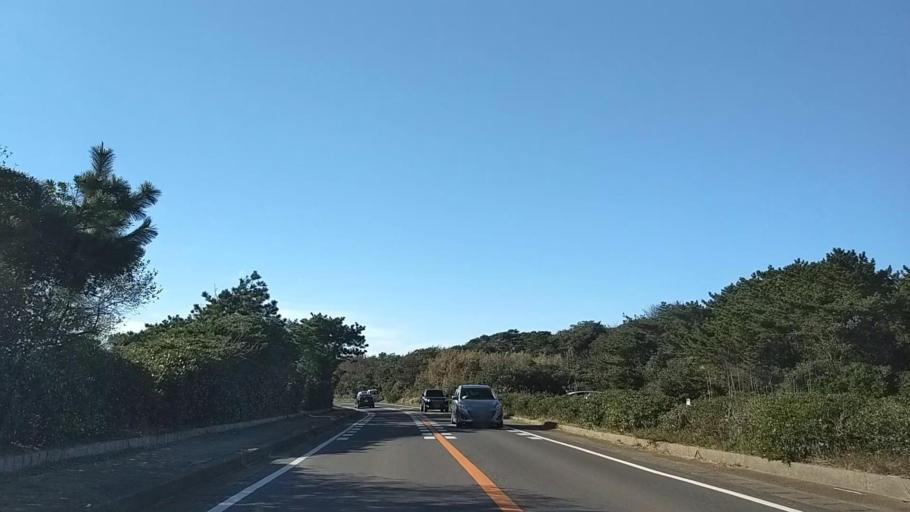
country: JP
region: Chiba
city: Hasaki
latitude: 35.7154
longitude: 140.8661
